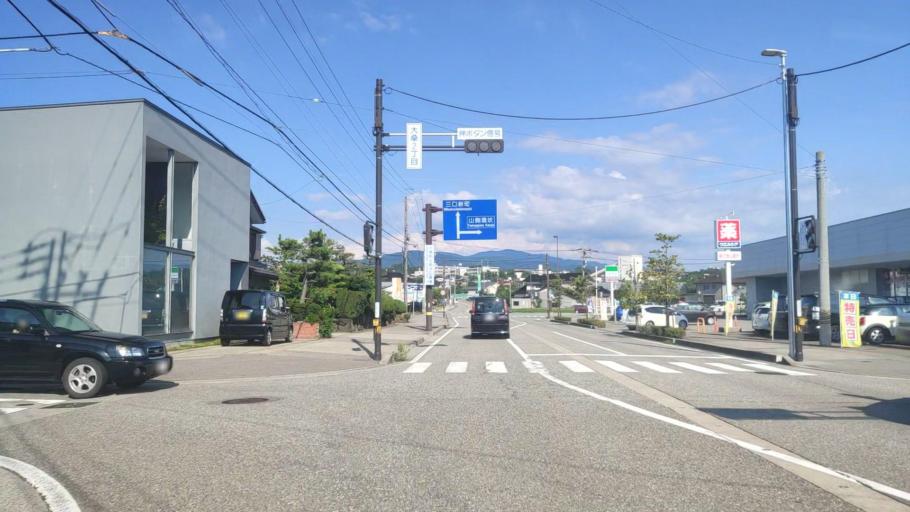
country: JP
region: Ishikawa
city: Nonoichi
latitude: 36.5387
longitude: 136.6738
